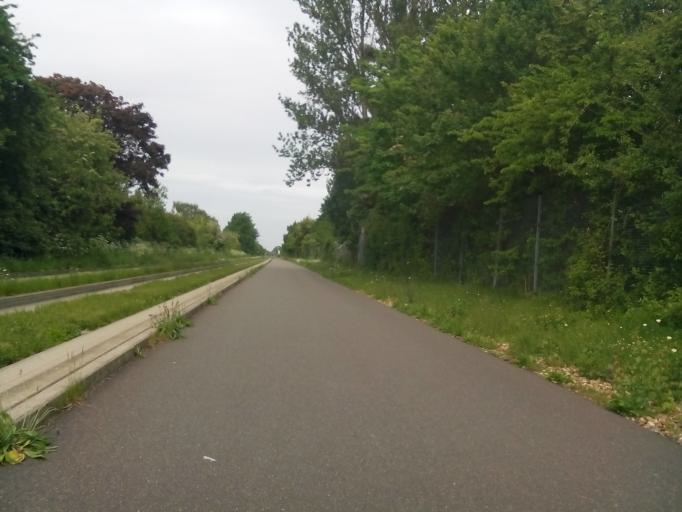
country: GB
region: England
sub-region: Cambridgeshire
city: Cambridge
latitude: 52.2310
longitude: 0.1438
